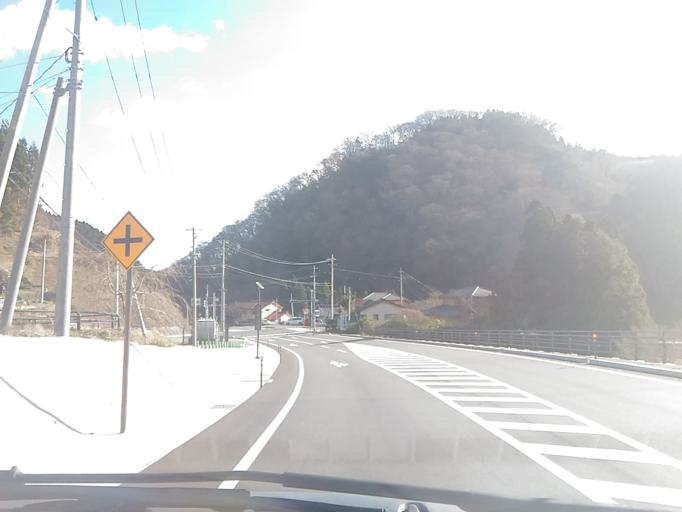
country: JP
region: Fukushima
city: Iwaki
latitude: 37.0029
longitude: 140.7080
